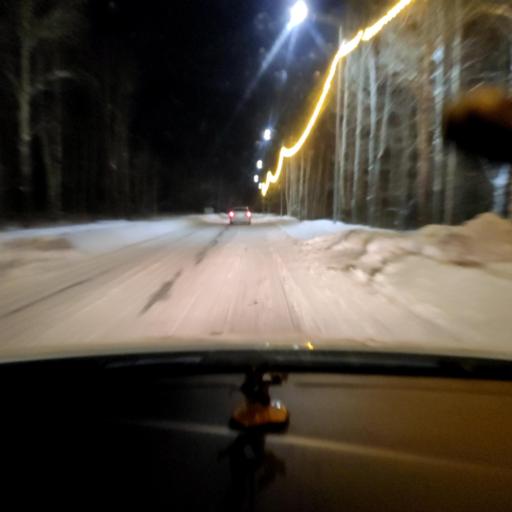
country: RU
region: Tatarstan
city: Stolbishchi
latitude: 55.6796
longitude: 49.1964
